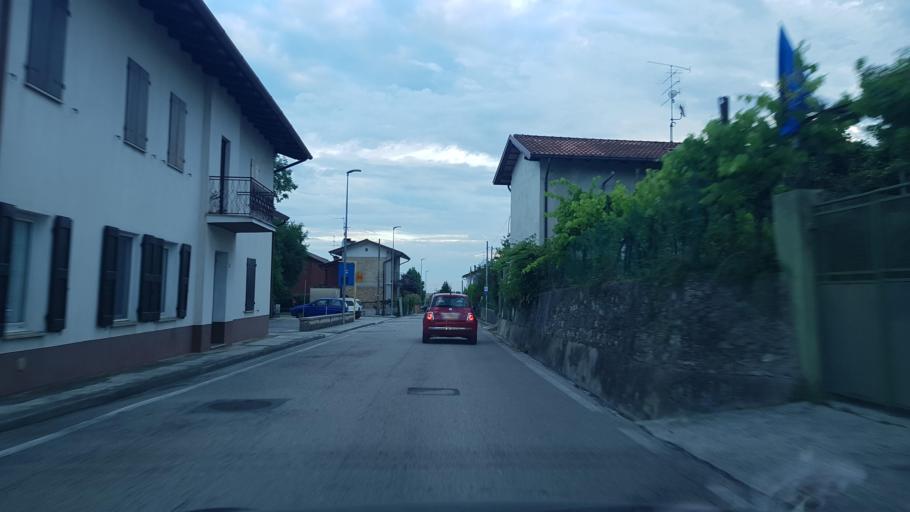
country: IT
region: Friuli Venezia Giulia
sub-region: Provincia di Pordenone
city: Pinzano al Tagliamento
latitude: 46.1844
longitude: 12.9631
